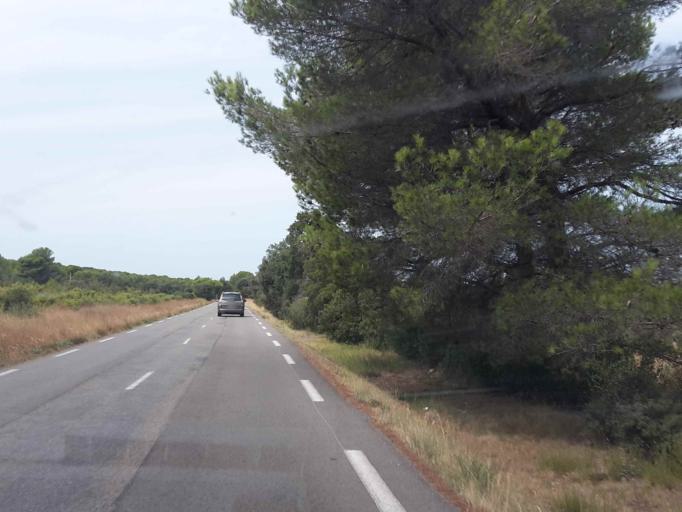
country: FR
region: Provence-Alpes-Cote d'Azur
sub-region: Departement des Bouches-du-Rhone
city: La Fare-les-Oliviers
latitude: 43.5837
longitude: 5.1898
